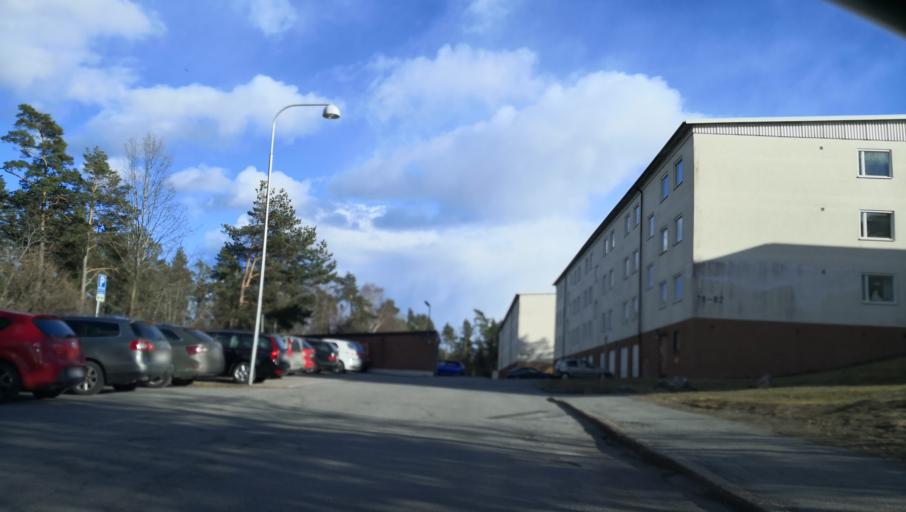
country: SE
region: Stockholm
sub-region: Varmdo Kommun
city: Gustavsberg
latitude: 59.3390
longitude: 18.3958
